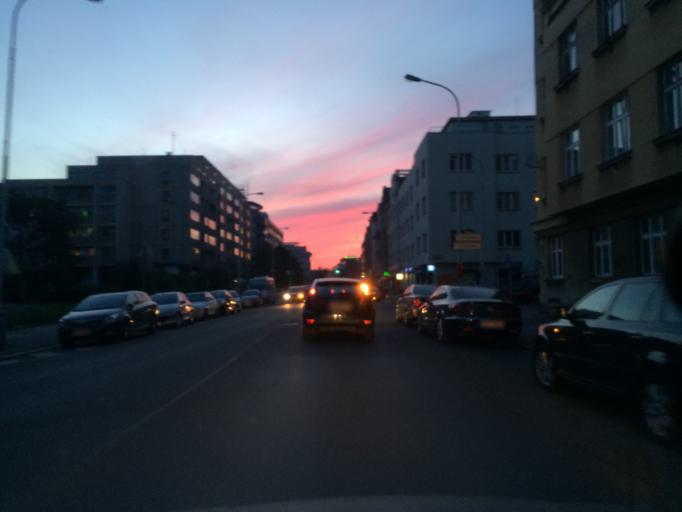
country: CZ
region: Praha
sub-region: Praha 2
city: Vysehrad
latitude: 50.0582
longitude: 14.4325
